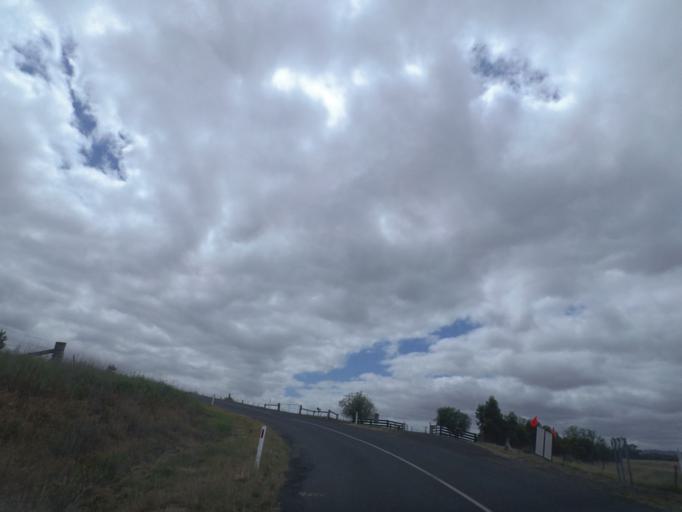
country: AU
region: Victoria
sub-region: Whittlesea
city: Whittlesea
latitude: -37.1100
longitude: 145.0245
